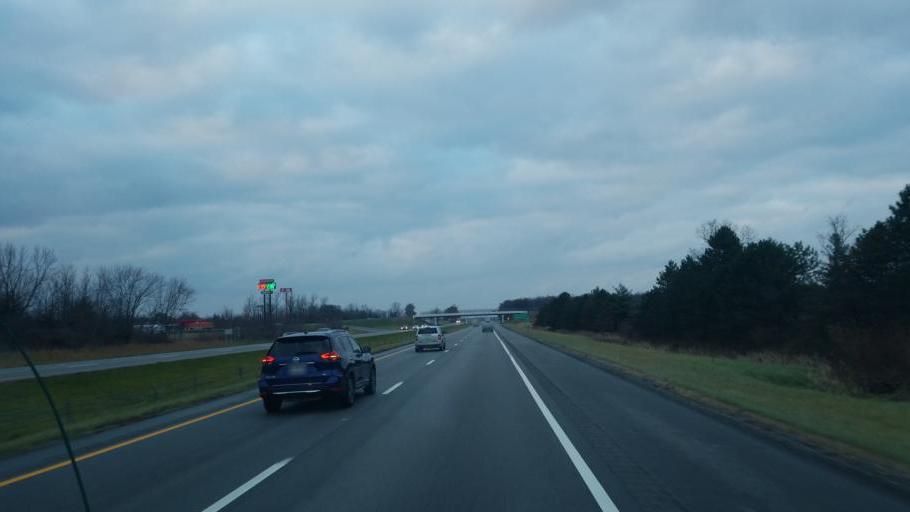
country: US
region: Ohio
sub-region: Auglaize County
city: Cridersville
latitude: 40.6505
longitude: -84.1311
